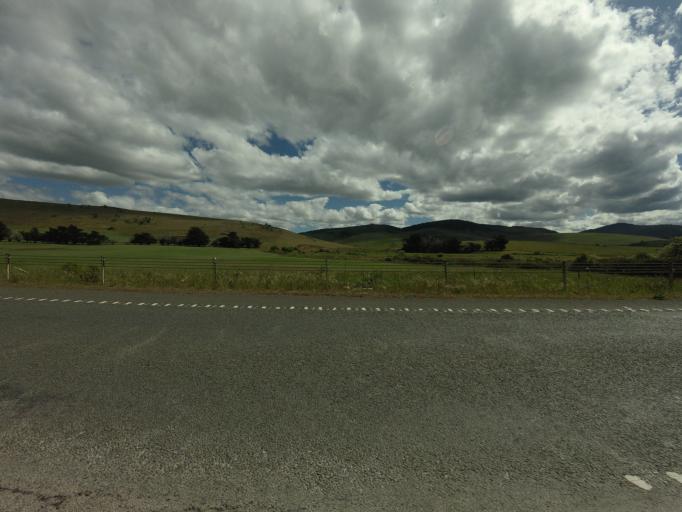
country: AU
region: Tasmania
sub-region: Brighton
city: Bridgewater
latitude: -42.1990
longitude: 147.3934
